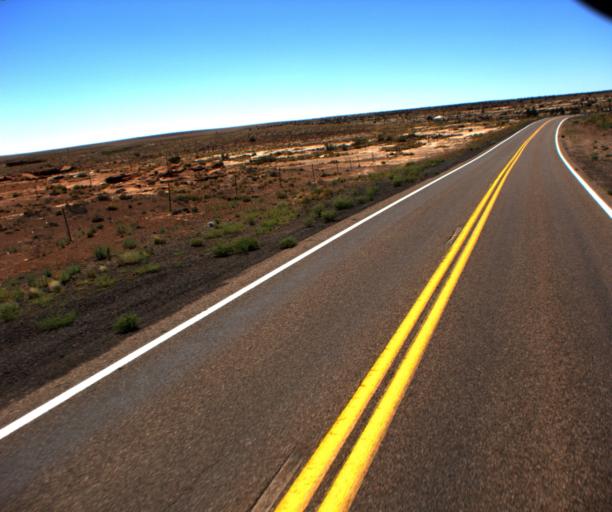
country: US
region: Arizona
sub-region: Navajo County
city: Winslow
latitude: 34.9721
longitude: -110.6489
